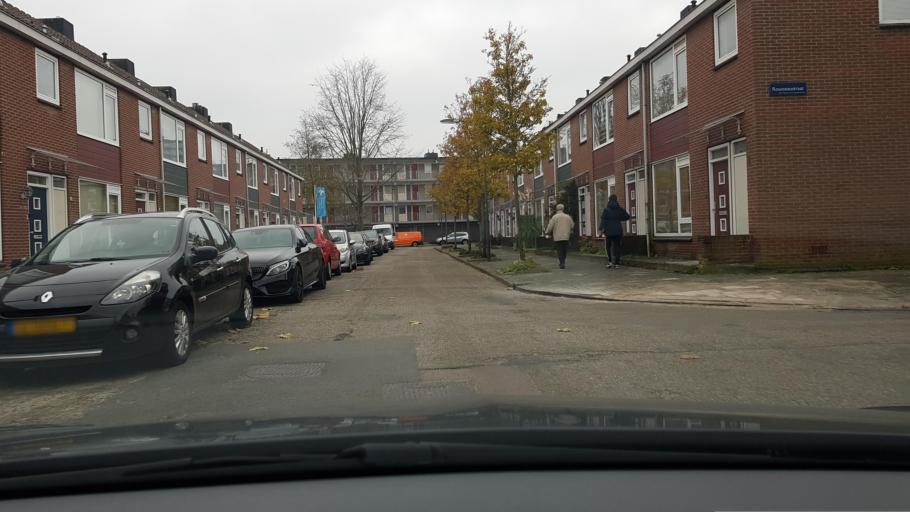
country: NL
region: North Holland
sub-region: Gemeente Haarlem
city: Haarlem
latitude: 52.3583
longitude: 4.6588
